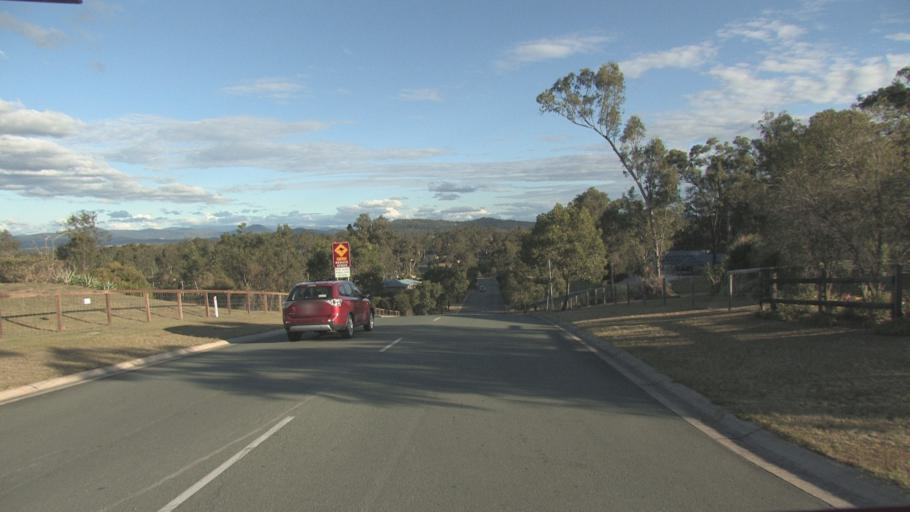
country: AU
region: Queensland
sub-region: Logan
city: Cedar Vale
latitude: -27.8677
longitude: 153.0770
